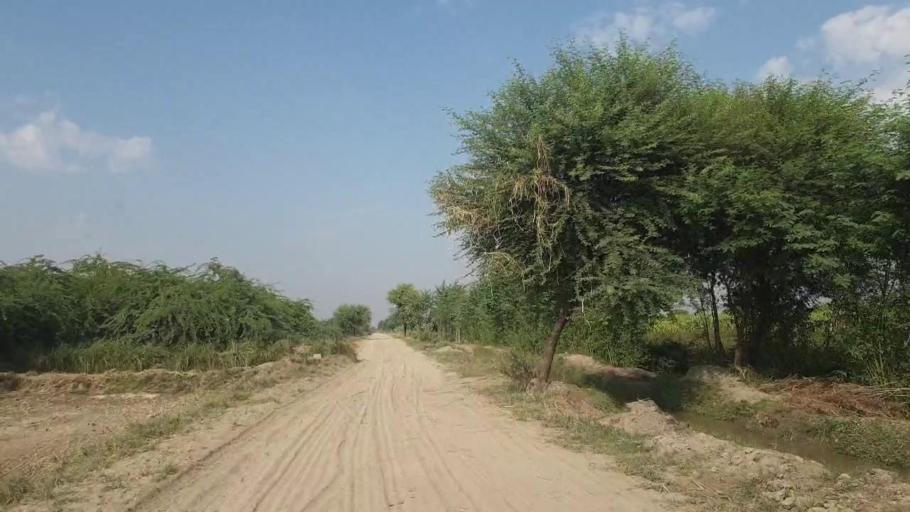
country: PK
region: Sindh
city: Digri
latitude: 25.0260
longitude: 69.0710
